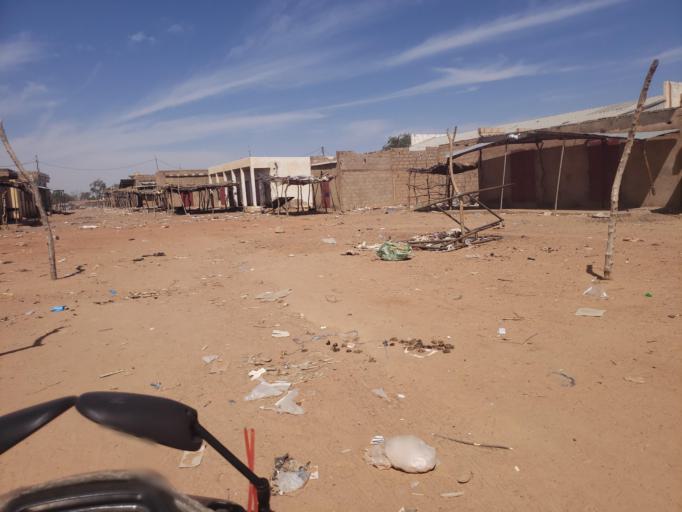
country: SN
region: Matam
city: Ranerou
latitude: 15.2957
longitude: -13.9613
